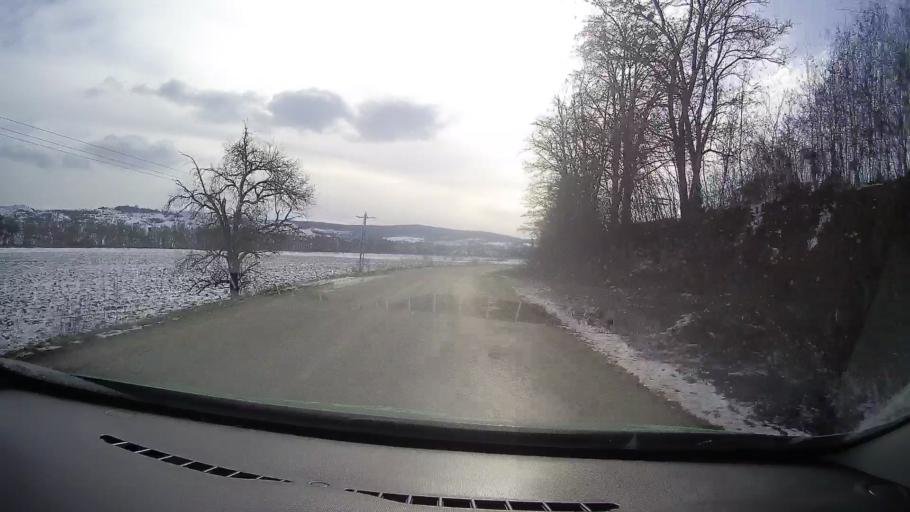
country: RO
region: Sibiu
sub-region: Comuna Iacobeni
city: Iacobeni
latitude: 46.0467
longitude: 24.7628
